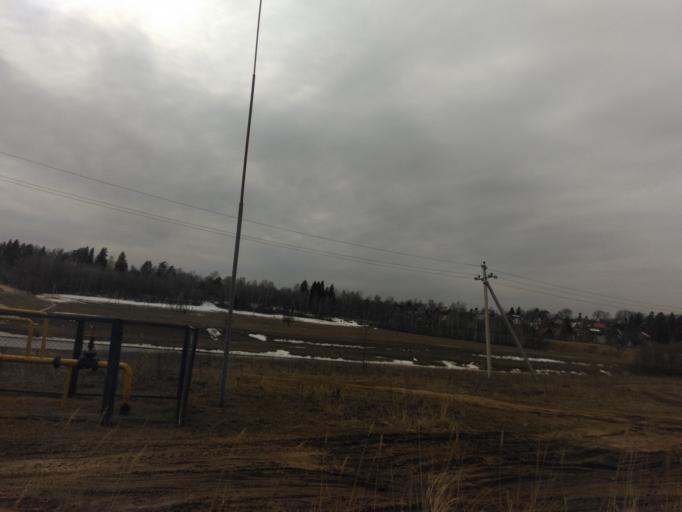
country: RU
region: Moskovskaya
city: Tuchkovo
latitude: 55.6121
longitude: 36.4241
